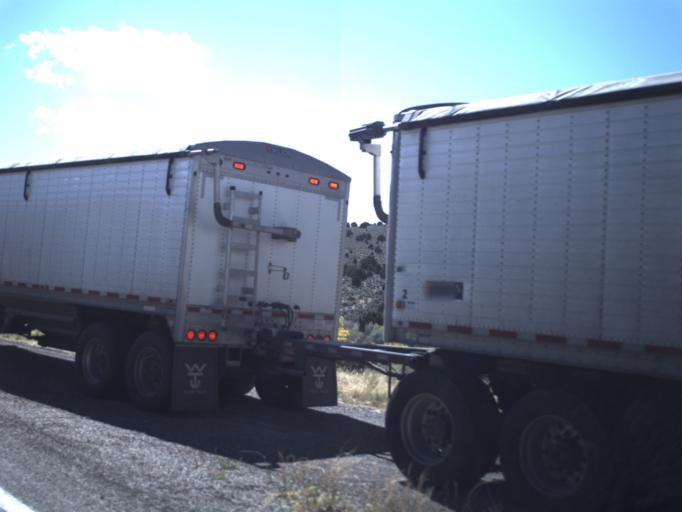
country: US
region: Utah
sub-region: Beaver County
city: Milford
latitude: 38.1136
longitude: -112.9517
